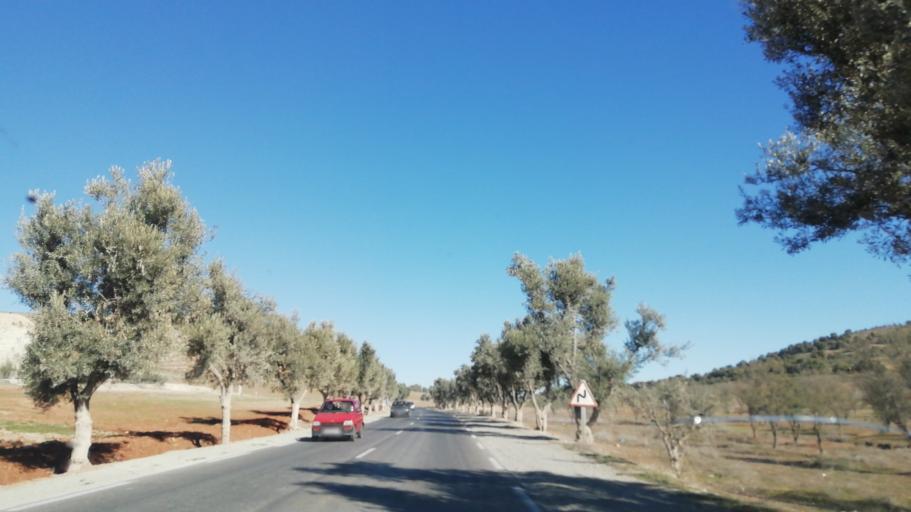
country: DZ
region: Mascara
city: Mascara
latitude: 35.2392
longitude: 0.1178
